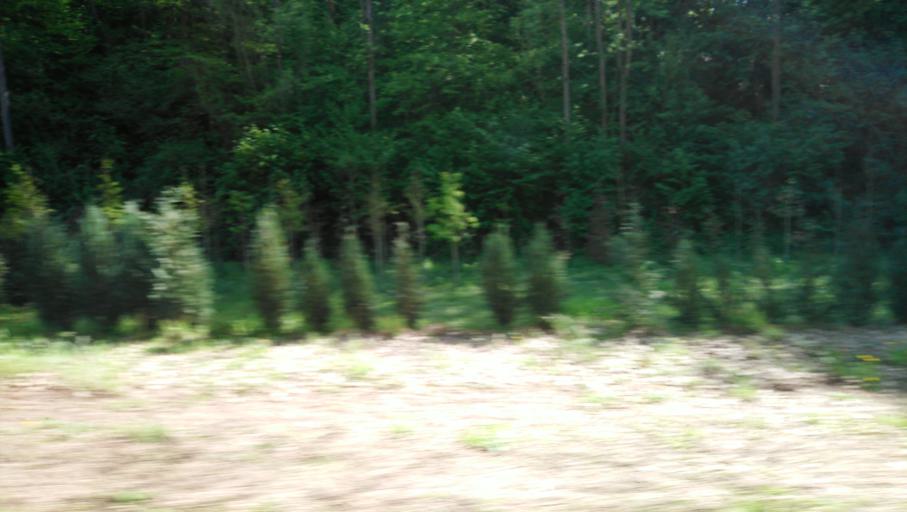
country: LU
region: Diekirch
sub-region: Canton de Vianden
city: Tandel
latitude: 49.8821
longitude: 6.1870
